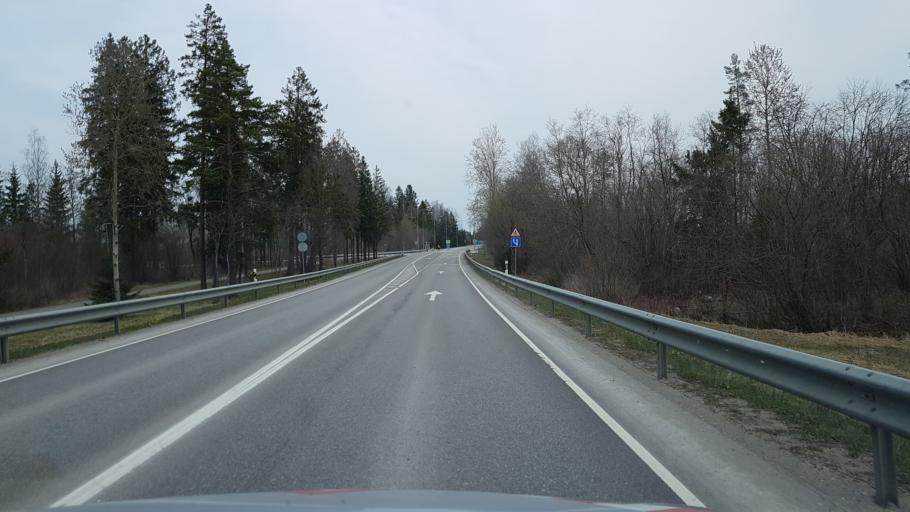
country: EE
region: Laeaene-Virumaa
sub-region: Someru vald
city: Someru
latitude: 59.3609
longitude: 26.4124
